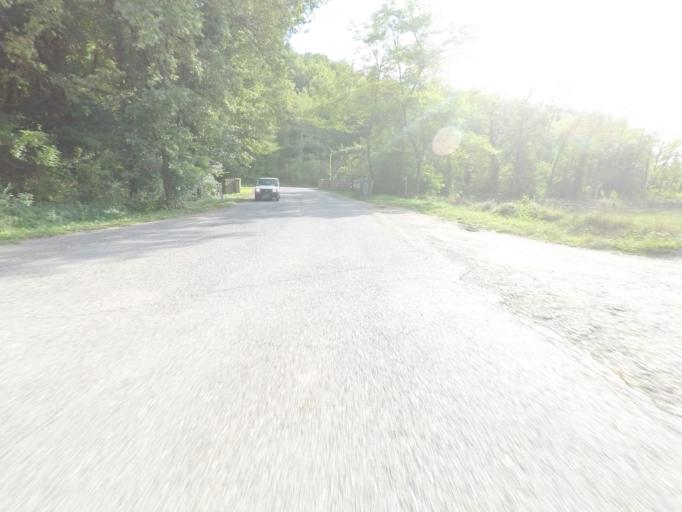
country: IT
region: Tuscany
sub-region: Provincia di Siena
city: Radda in Chianti
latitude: 43.5105
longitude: 11.4056
